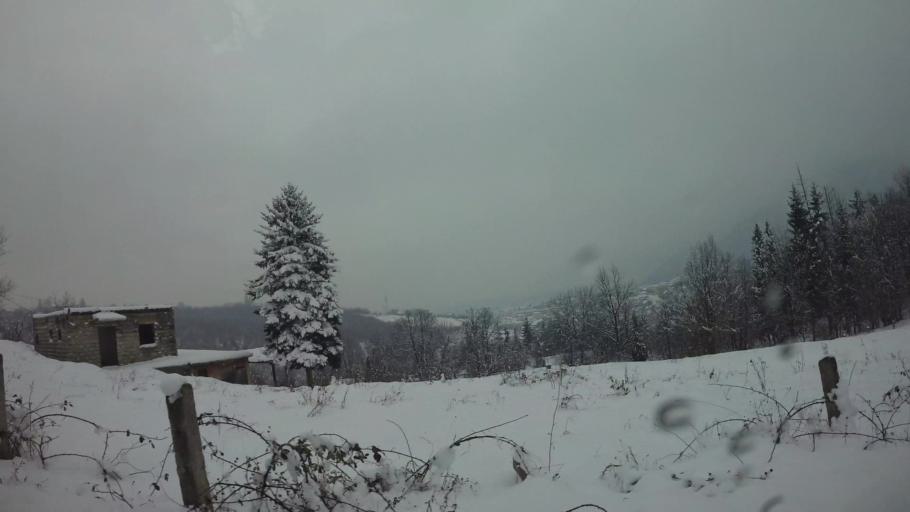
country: BA
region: Federation of Bosnia and Herzegovina
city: Hadzici
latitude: 43.8496
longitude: 18.2590
